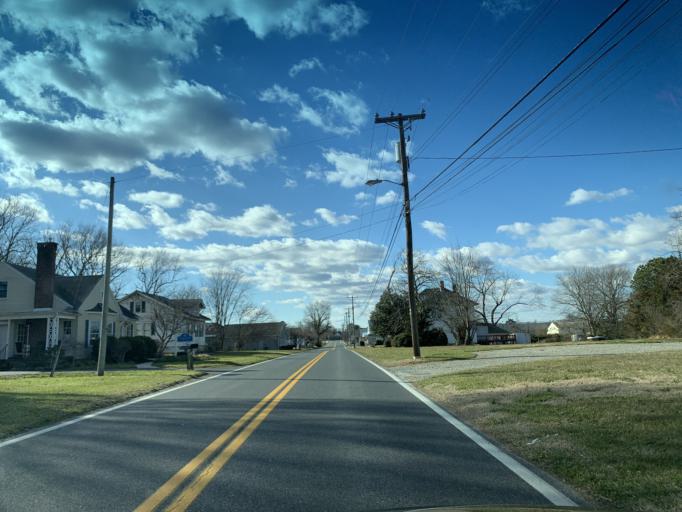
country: US
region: Maryland
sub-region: Worcester County
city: Berlin
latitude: 38.3341
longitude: -75.2142
